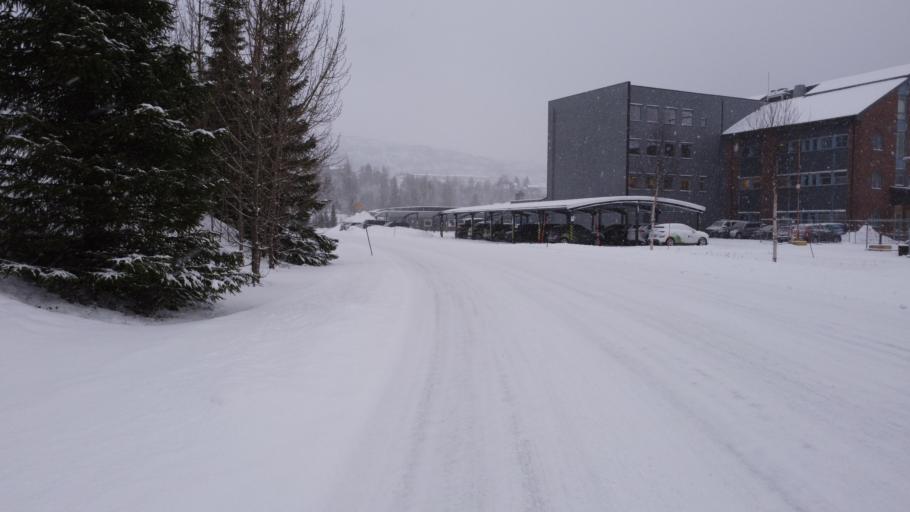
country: NO
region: Nordland
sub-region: Rana
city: Mo i Rana
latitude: 66.3206
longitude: 14.1541
